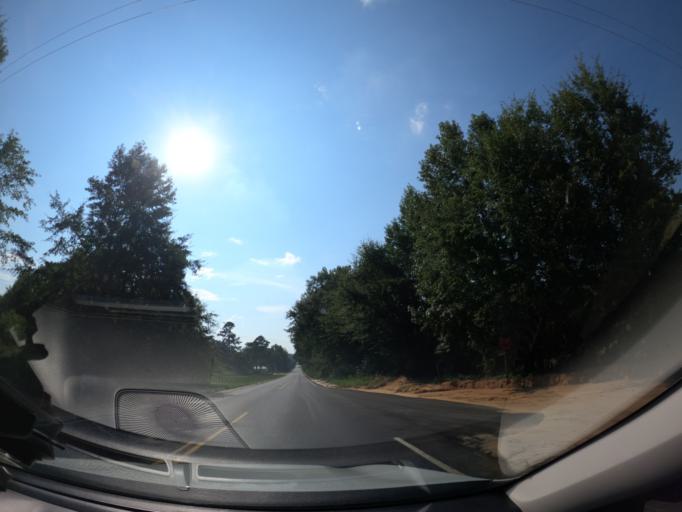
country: US
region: South Carolina
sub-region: Aiken County
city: Jackson
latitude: 33.4058
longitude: -81.7812
